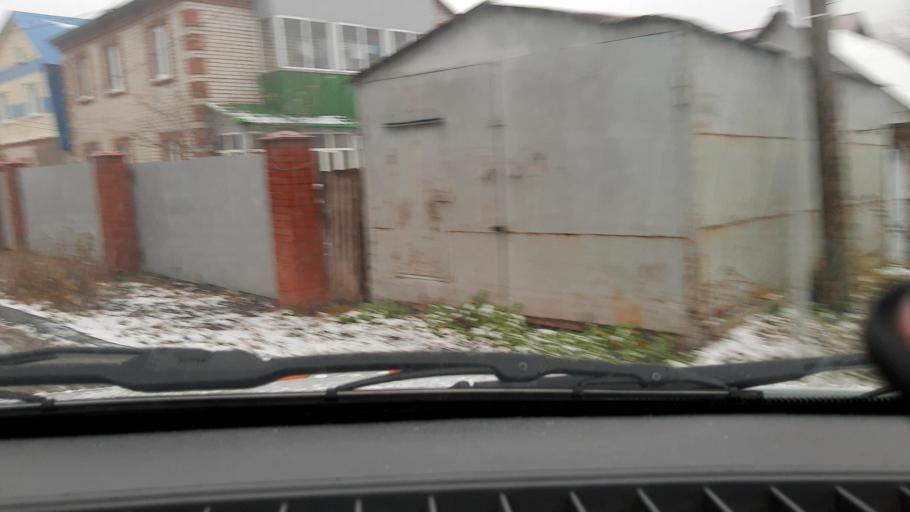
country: RU
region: Bashkortostan
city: Ufa
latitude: 54.7214
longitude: 55.9223
